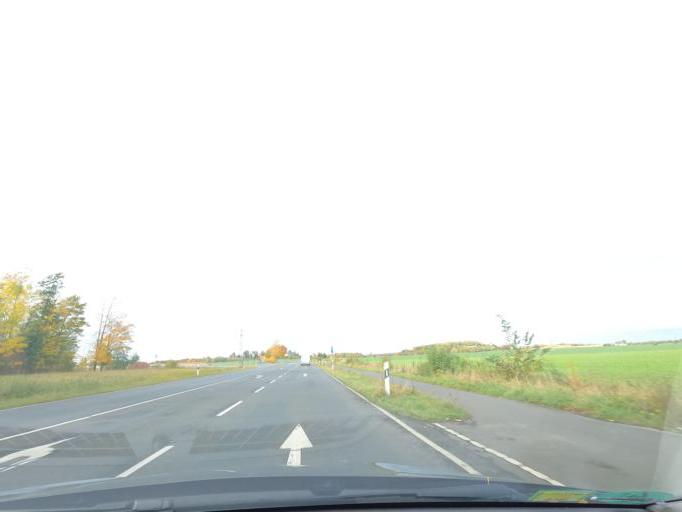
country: DE
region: Lower Saxony
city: Leiferde
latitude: 52.1782
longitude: 10.5063
